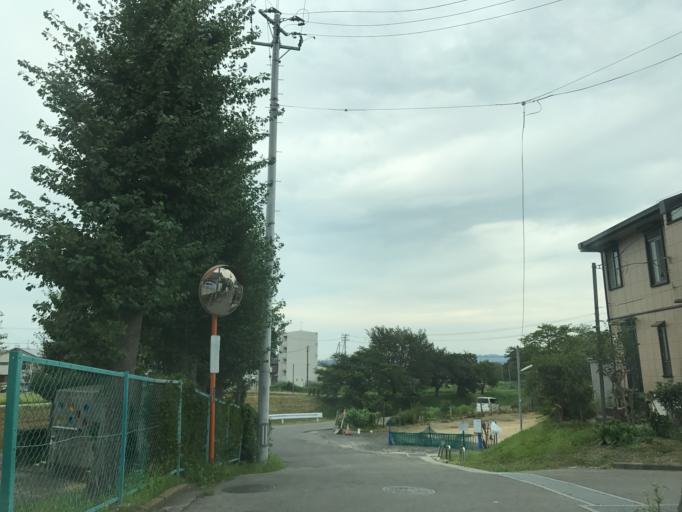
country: JP
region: Fukushima
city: Koriyama
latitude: 37.4114
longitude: 140.3707
